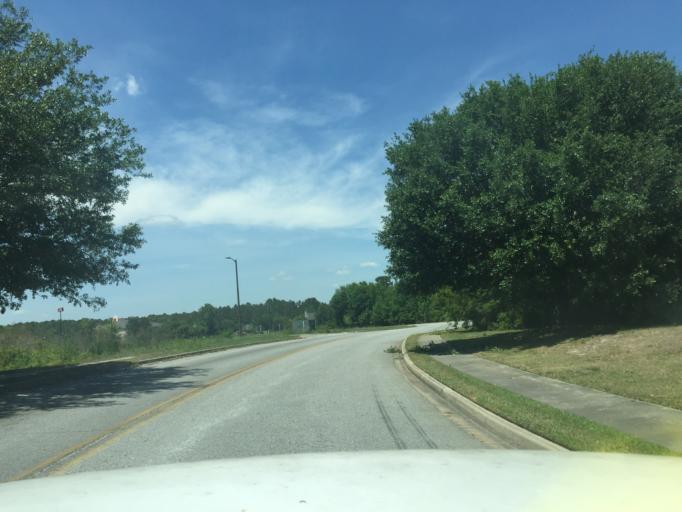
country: US
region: Georgia
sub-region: Chatham County
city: Georgetown
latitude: 32.0044
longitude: -81.2744
